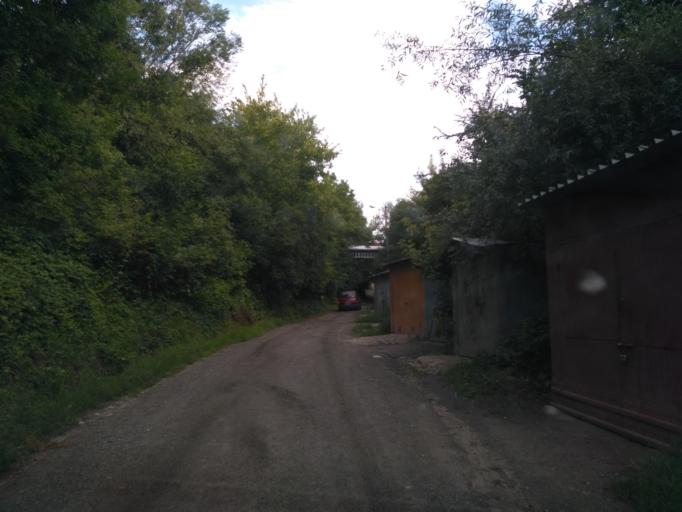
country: PL
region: Subcarpathian Voivodeship
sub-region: Przemysl
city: Przemysl
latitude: 49.7876
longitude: 22.7547
